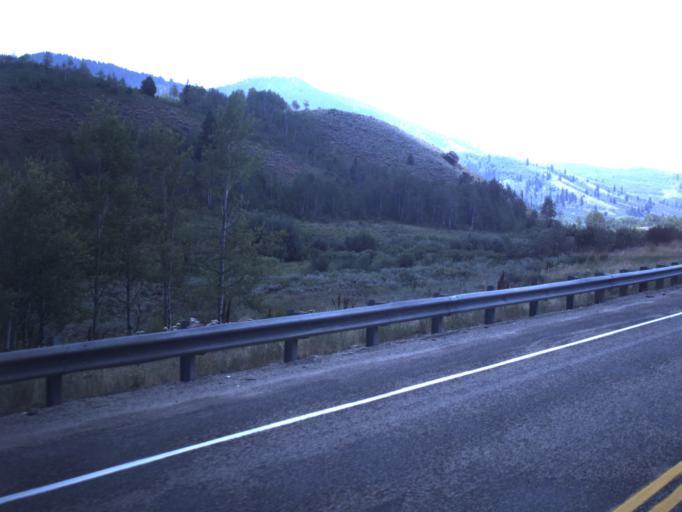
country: US
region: Utah
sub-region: Cache County
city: Richmond
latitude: 41.8945
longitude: -111.5655
